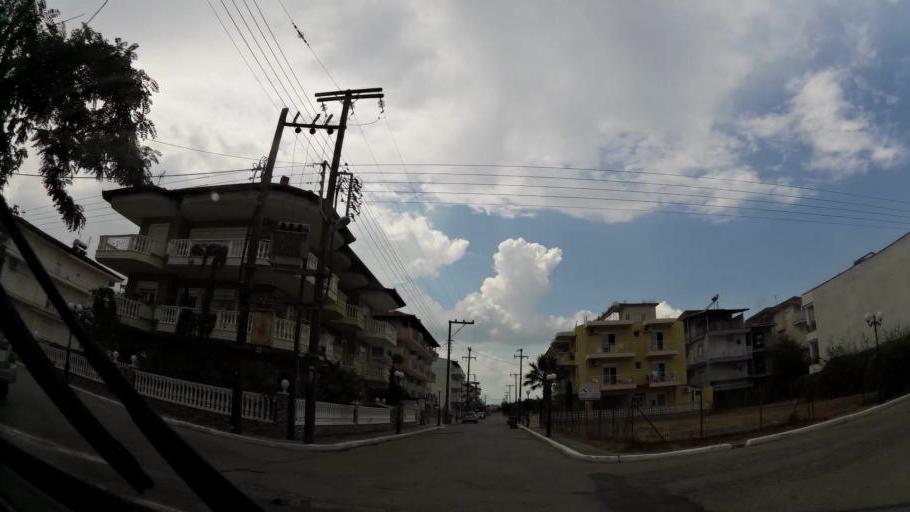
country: GR
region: Central Macedonia
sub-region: Nomos Pierias
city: Paralia
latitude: 40.2729
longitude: 22.5989
